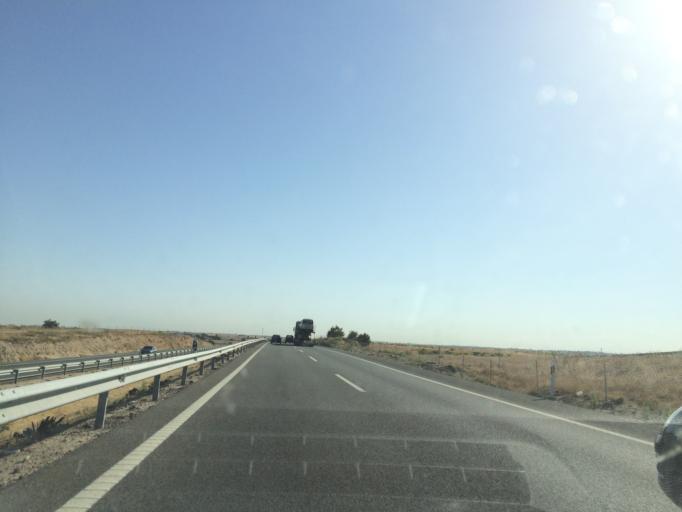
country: ES
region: Castille-La Mancha
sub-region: Province of Toledo
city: La Torre de Esteban Hambran
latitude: 40.1454
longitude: -4.1851
